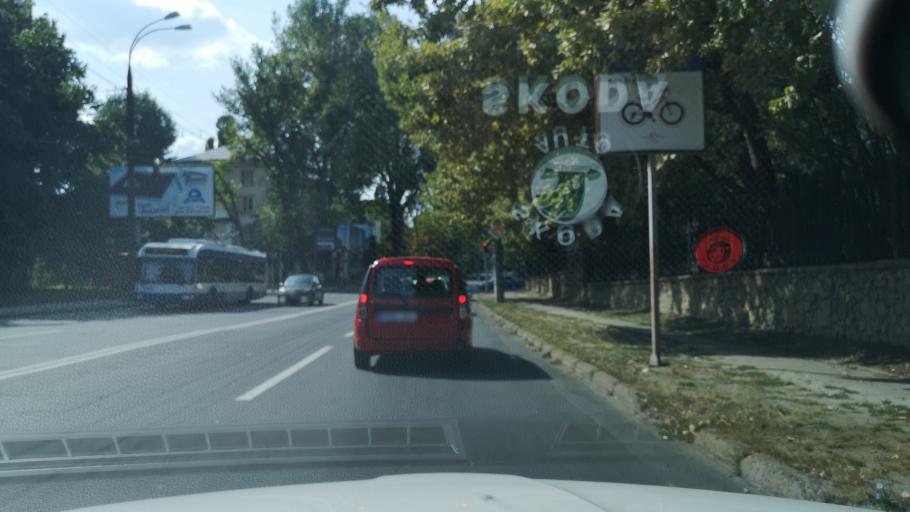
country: MD
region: Chisinau
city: Chisinau
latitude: 47.0224
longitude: 28.8104
